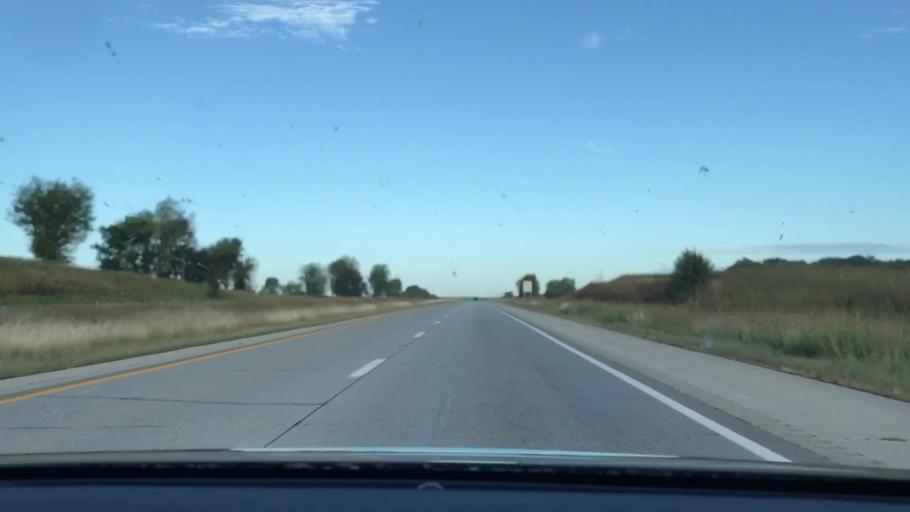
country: US
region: Kentucky
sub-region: Christian County
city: Hopkinsville
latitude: 36.8191
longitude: -87.6435
